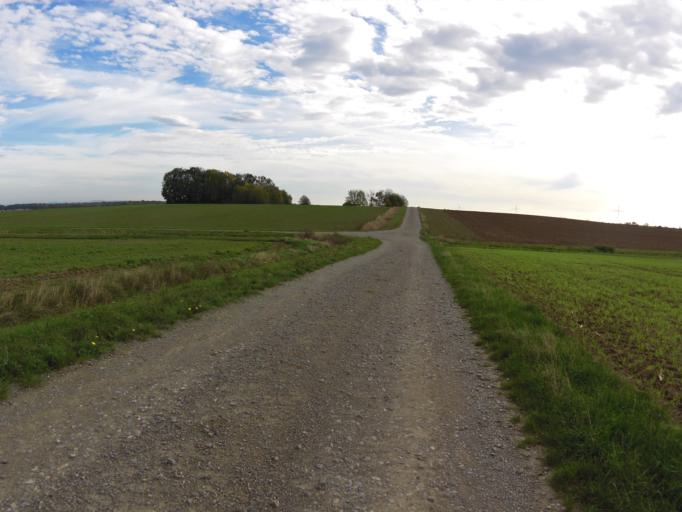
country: DE
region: Bavaria
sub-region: Regierungsbezirk Unterfranken
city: Biebelried
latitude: 49.7328
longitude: 10.0731
